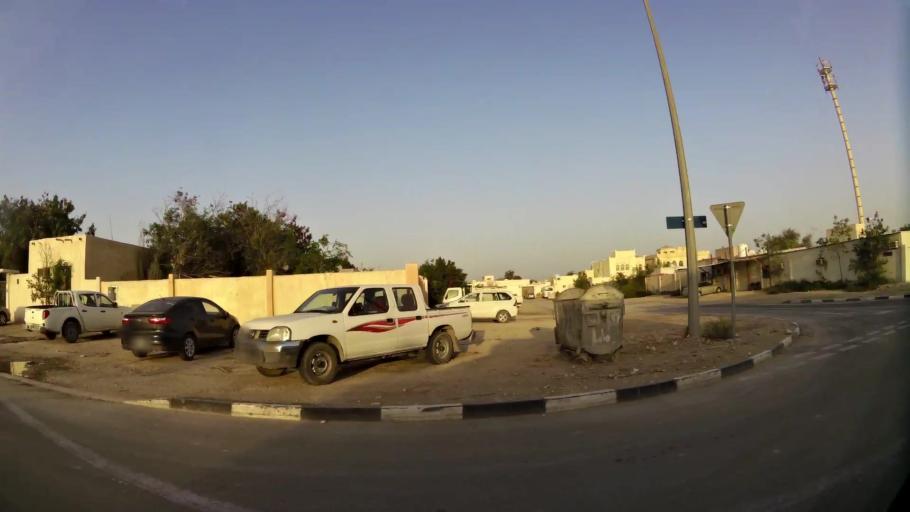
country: QA
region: Baladiyat ar Rayyan
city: Ar Rayyan
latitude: 25.3142
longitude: 51.4533
